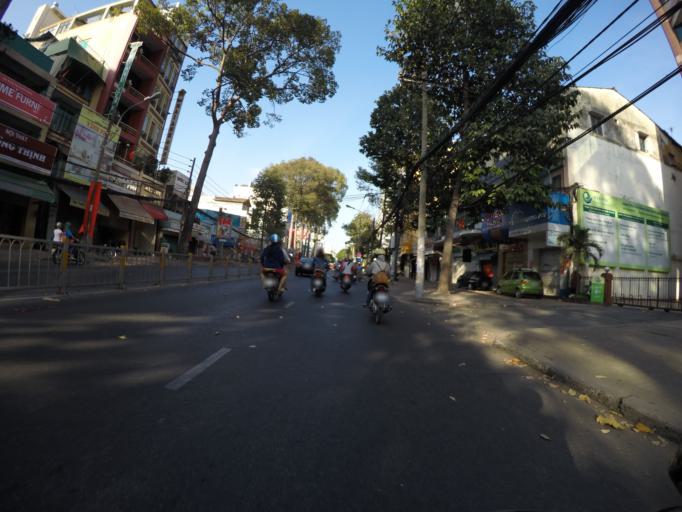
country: VN
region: Ho Chi Minh City
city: Quan Ba
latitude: 10.7724
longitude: 106.6884
